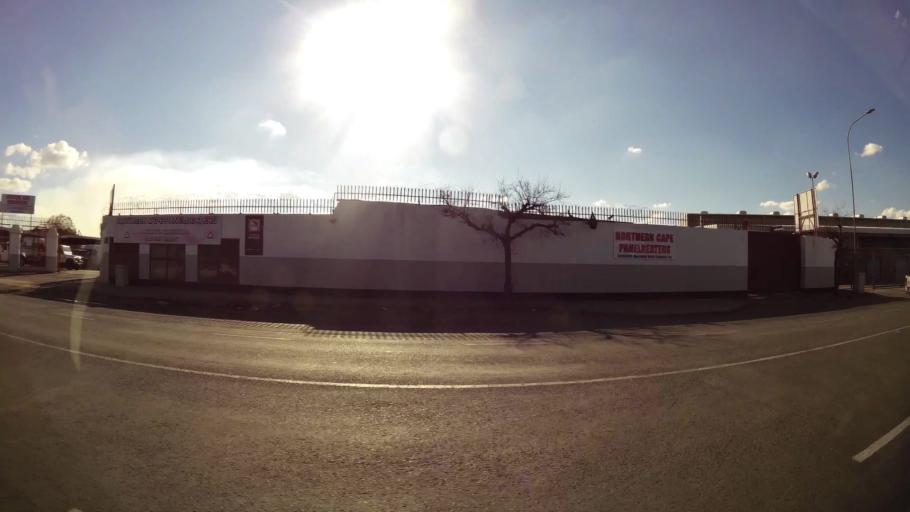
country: ZA
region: Northern Cape
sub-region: Frances Baard District Municipality
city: Kimberley
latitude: -28.7311
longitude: 24.7611
